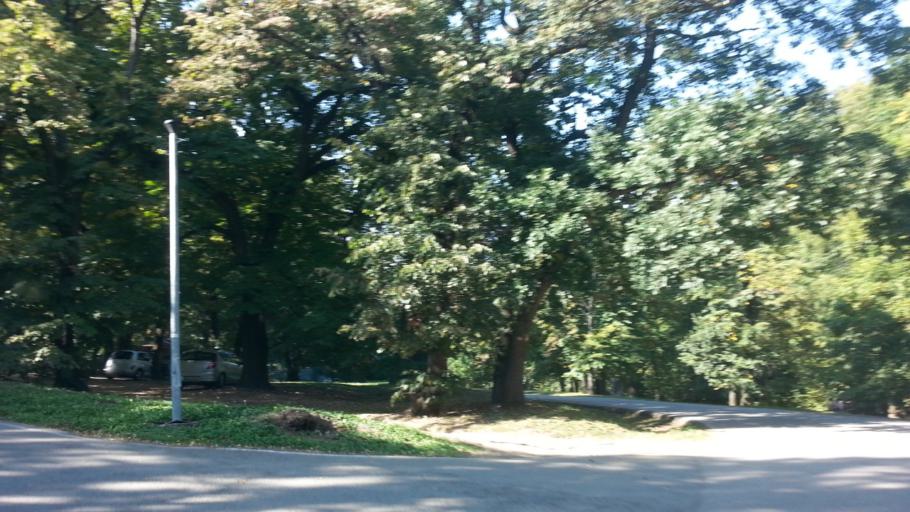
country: RS
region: Central Serbia
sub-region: Belgrade
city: Cukarica
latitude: 44.7712
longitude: 20.4300
